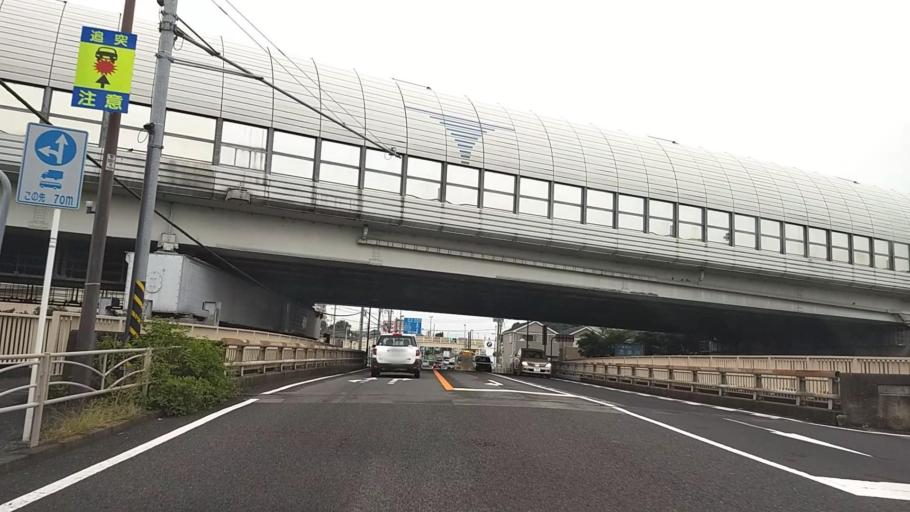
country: JP
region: Kanagawa
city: Atsugi
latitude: 35.4248
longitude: 139.3498
